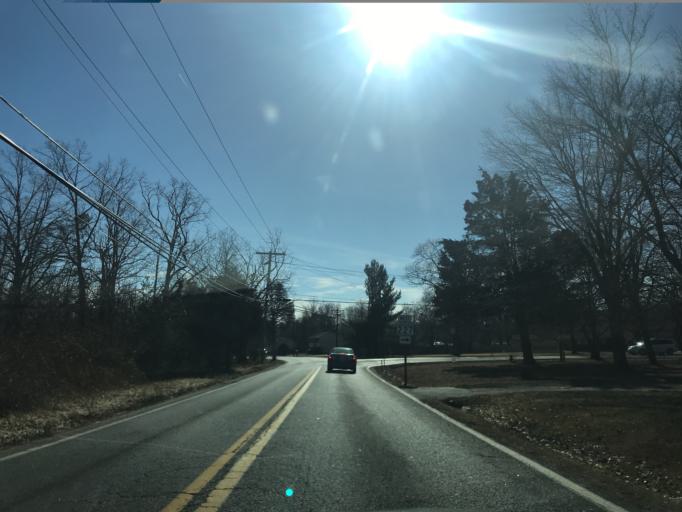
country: US
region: Maryland
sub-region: Charles County
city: Bennsville
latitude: 38.5781
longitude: -77.0310
